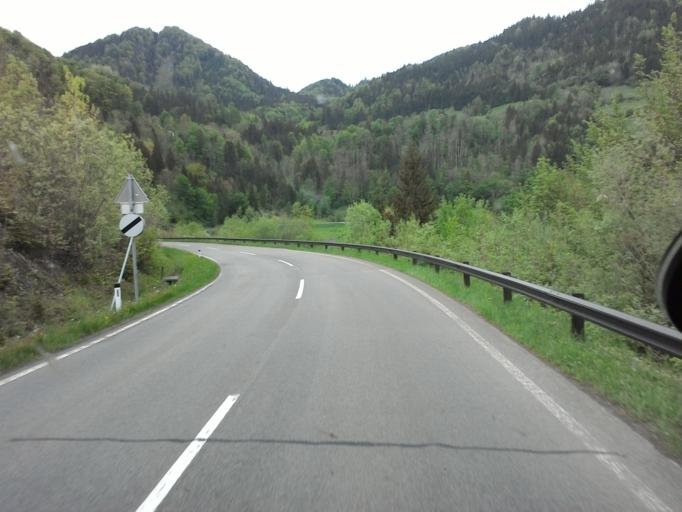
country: AT
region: Styria
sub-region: Politischer Bezirk Liezen
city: Altenmarkt bei Sankt Gallen
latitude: 47.7199
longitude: 14.6669
